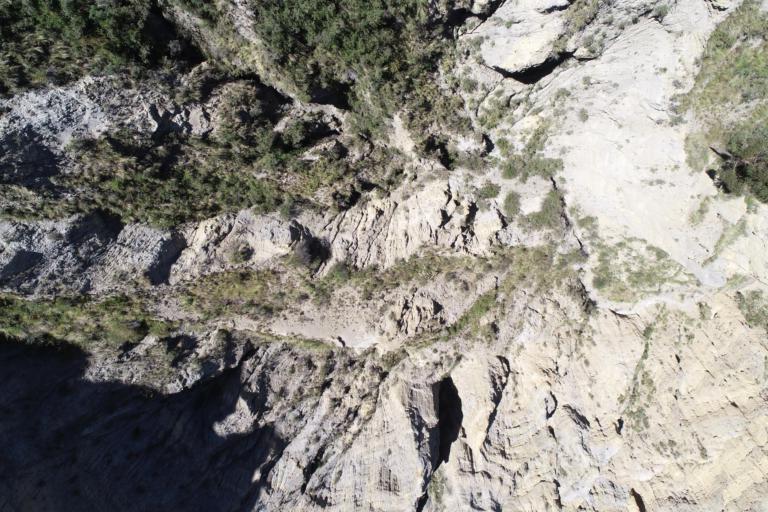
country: BO
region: La Paz
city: La Paz
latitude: -16.5033
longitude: -68.0660
